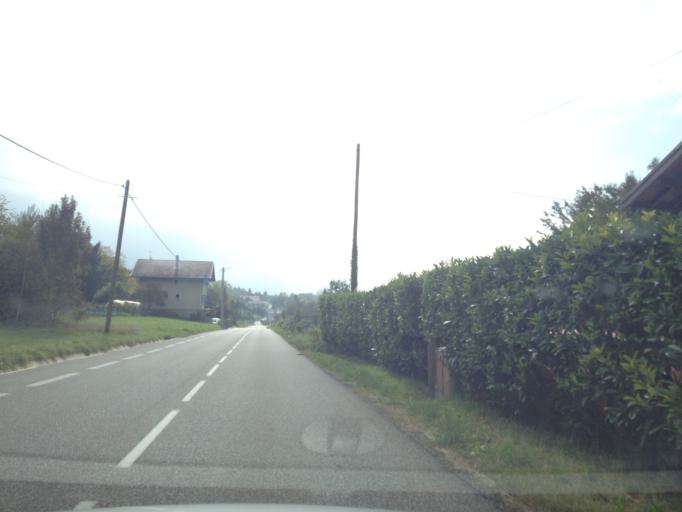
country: FR
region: Rhone-Alpes
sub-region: Departement de la Savoie
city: Mouxy
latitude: 45.6873
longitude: 5.9388
